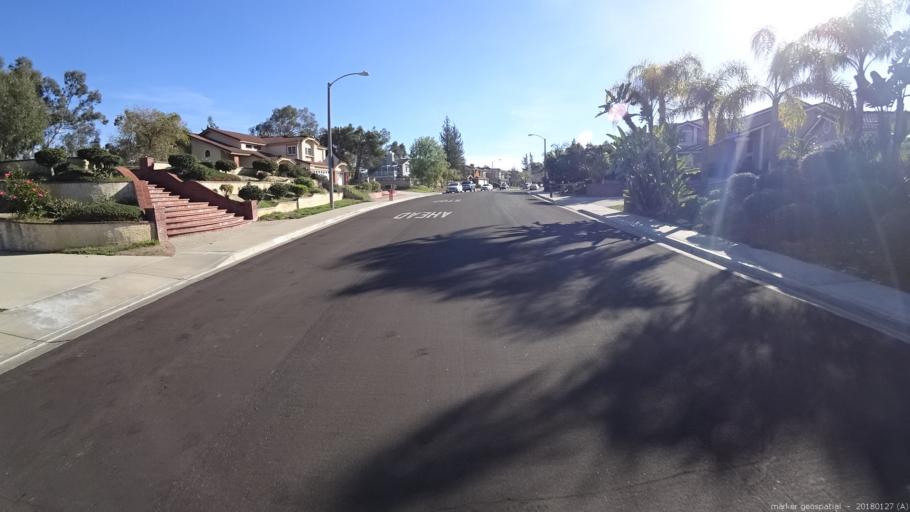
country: US
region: California
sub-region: Los Angeles County
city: Diamond Bar
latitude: 34.0147
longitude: -117.7987
